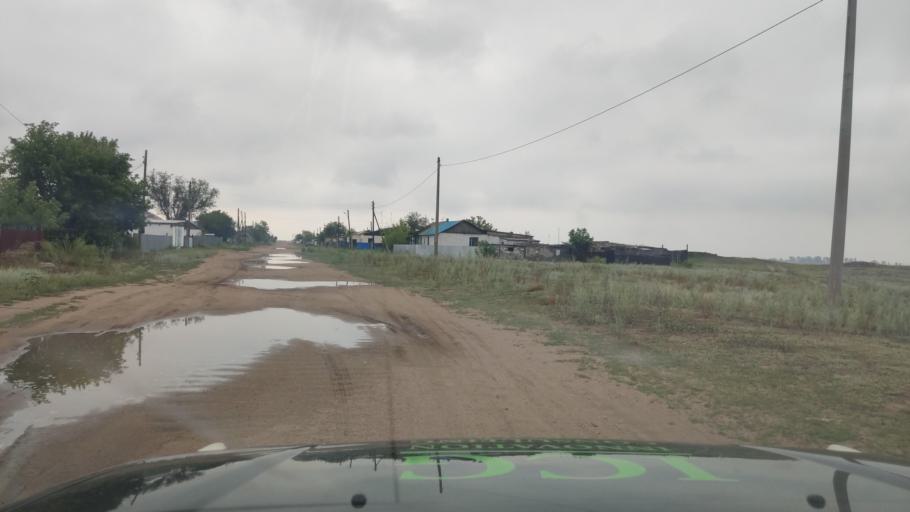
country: KZ
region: Pavlodar
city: Aksu
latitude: 52.0826
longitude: 77.1165
